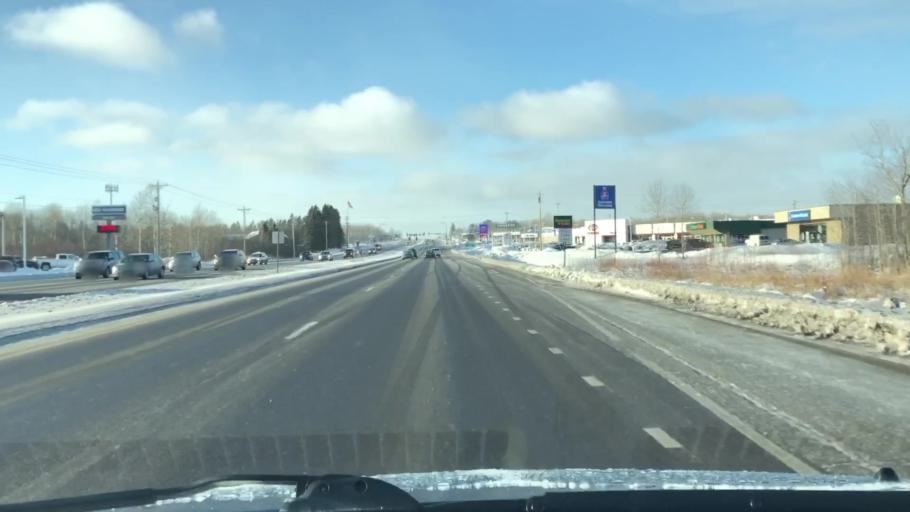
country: US
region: Minnesota
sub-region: Saint Louis County
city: Hermantown
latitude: 46.8195
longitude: -92.1822
